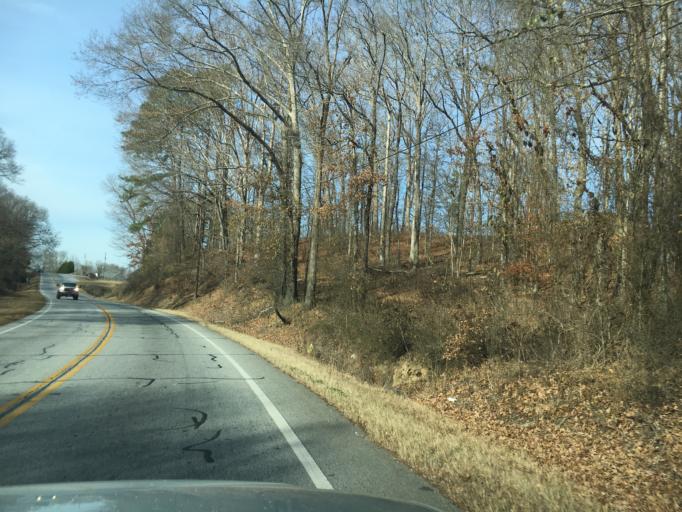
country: US
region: Georgia
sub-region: Jackson County
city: Hoschton
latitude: 34.0642
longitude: -83.7199
